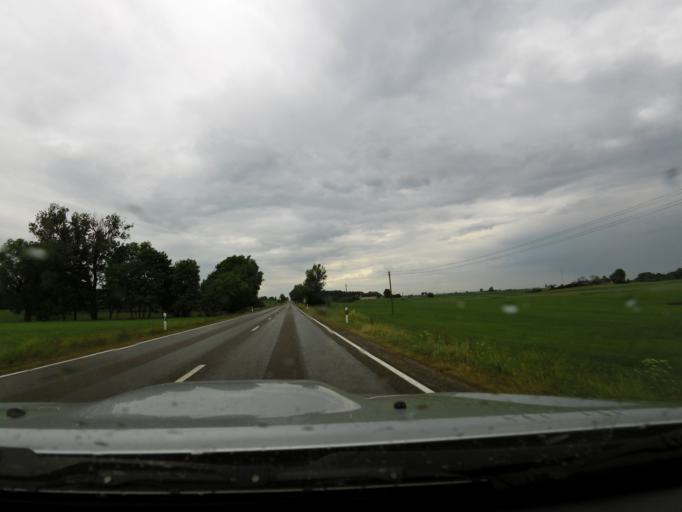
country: LT
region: Marijampoles apskritis
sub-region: Marijampole Municipality
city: Marijampole
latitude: 54.5481
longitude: 23.4720
